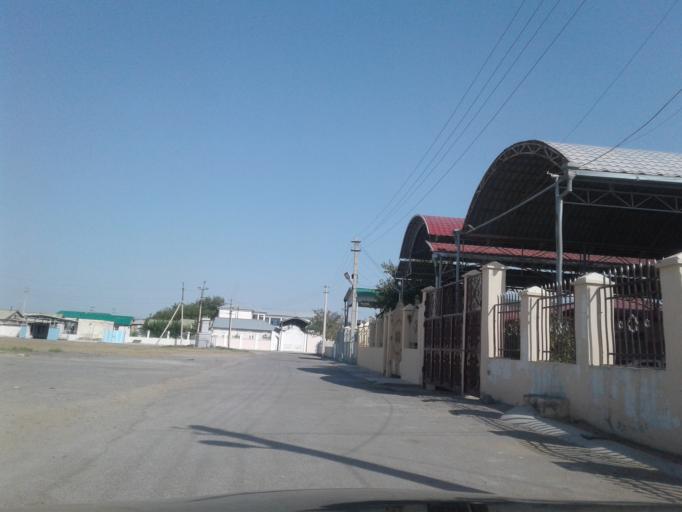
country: TM
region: Ahal
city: Ashgabat
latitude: 37.9735
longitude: 58.4365
